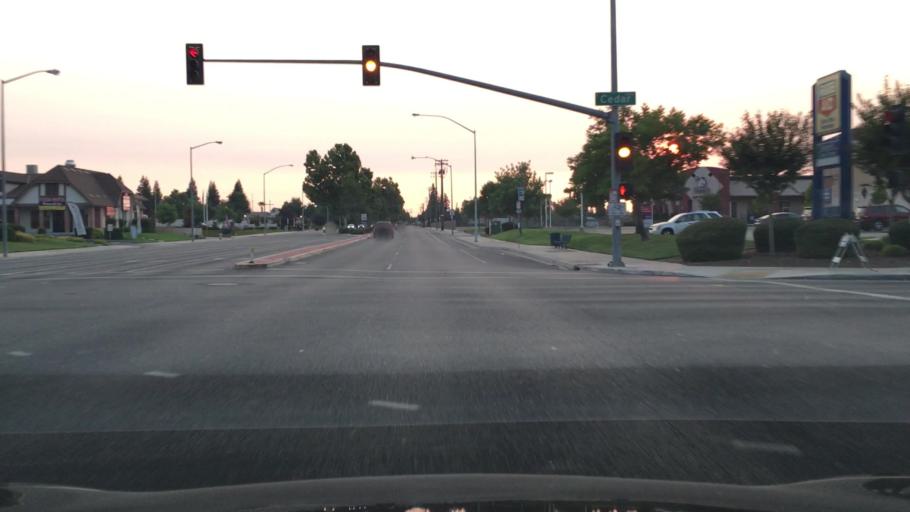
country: US
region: California
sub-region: Fresno County
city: Clovis
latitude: 36.8521
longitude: -119.7568
